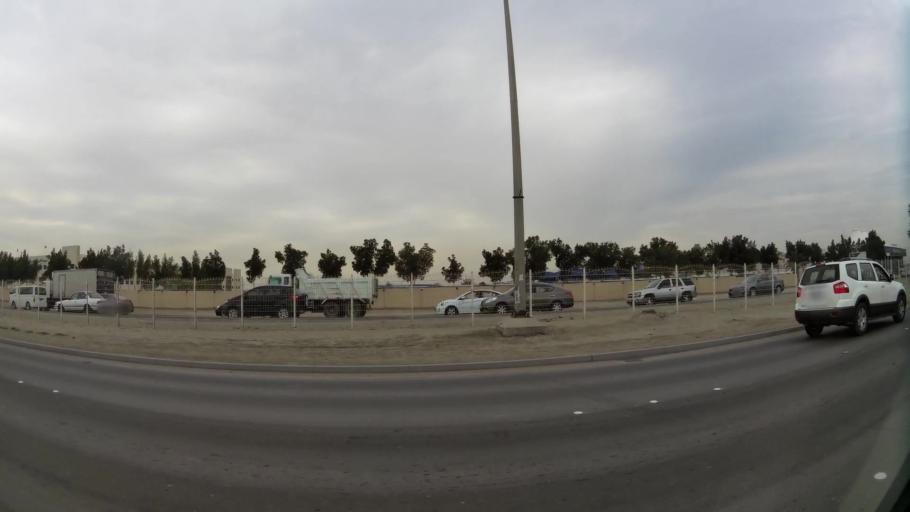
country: BH
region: Northern
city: Sitrah
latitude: 26.1677
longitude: 50.6043
